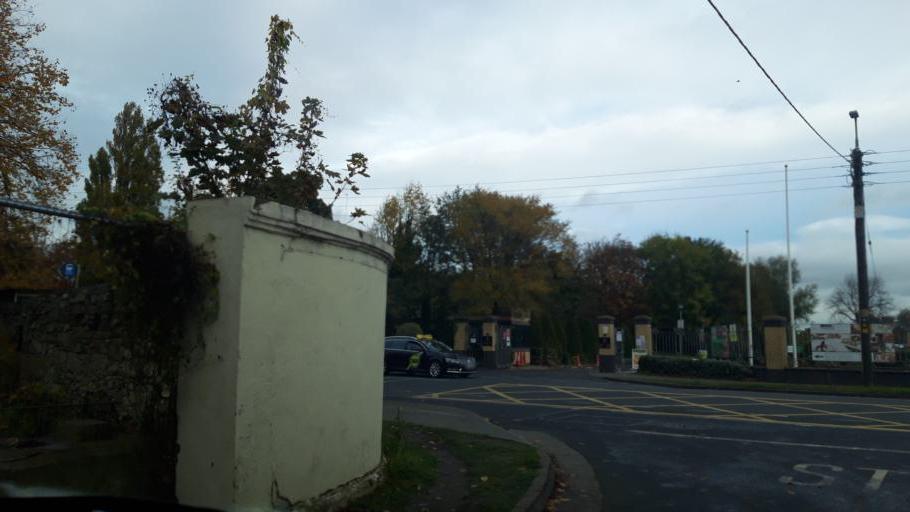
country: IE
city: Clonskeagh
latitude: 53.3043
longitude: -6.2355
